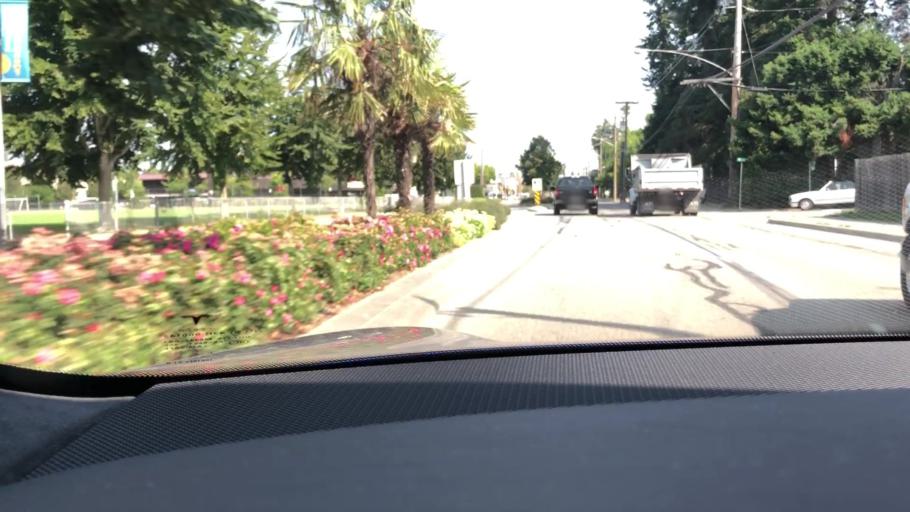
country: US
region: Washington
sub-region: Whatcom County
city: Point Roberts
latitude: 49.0208
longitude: -123.0686
